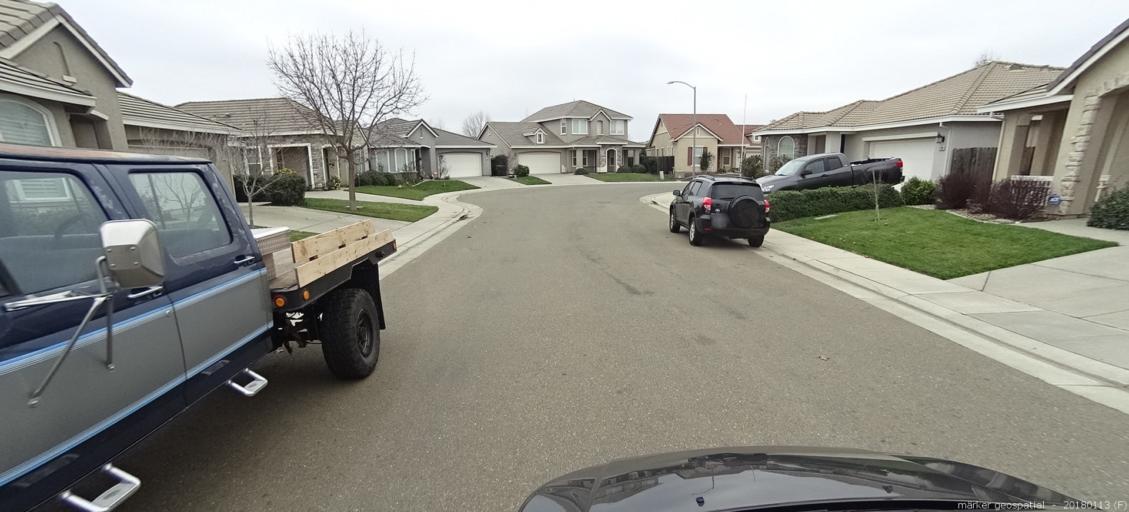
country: US
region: California
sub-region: Sacramento County
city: Gold River
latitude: 38.5523
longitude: -121.2151
